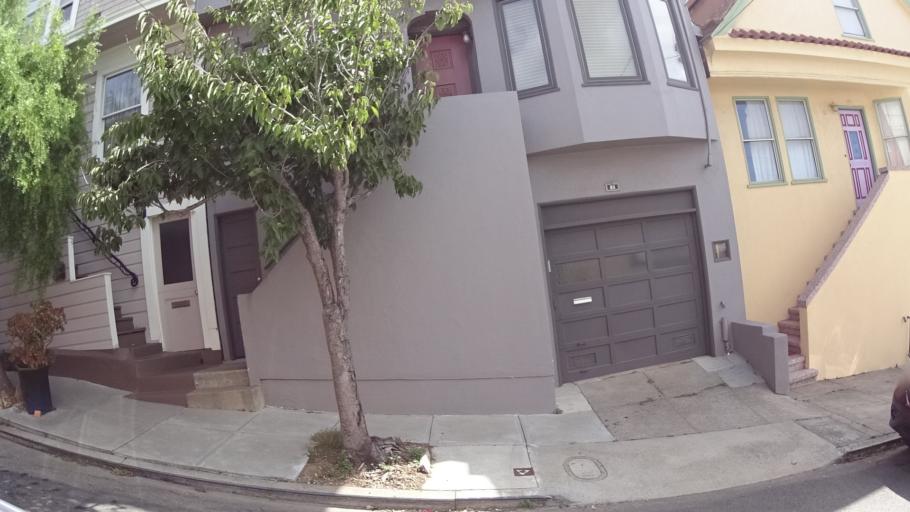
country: US
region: California
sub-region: San Francisco County
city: San Francisco
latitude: 37.7407
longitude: -122.4170
